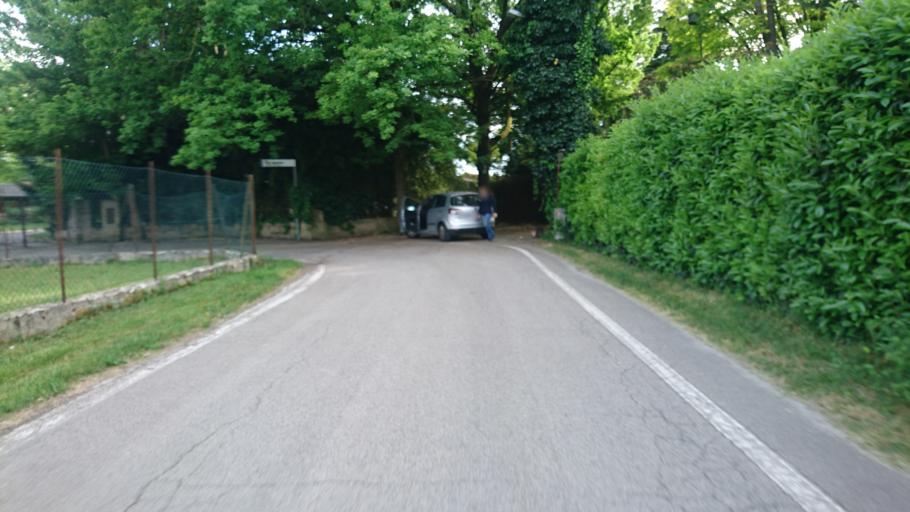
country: IT
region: Veneto
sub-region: Provincia di Padova
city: Mandriola-Sant'Agostino
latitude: 45.3801
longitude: 11.8429
